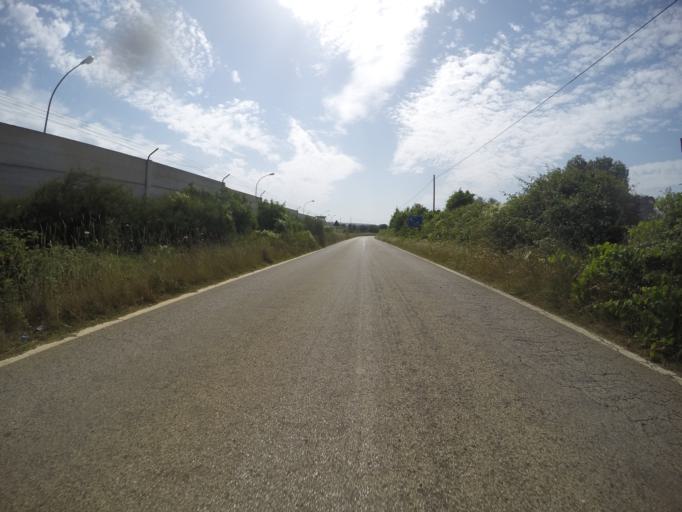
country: IT
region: Apulia
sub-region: Provincia di Taranto
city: Montemesola
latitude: 40.6038
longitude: 17.3751
